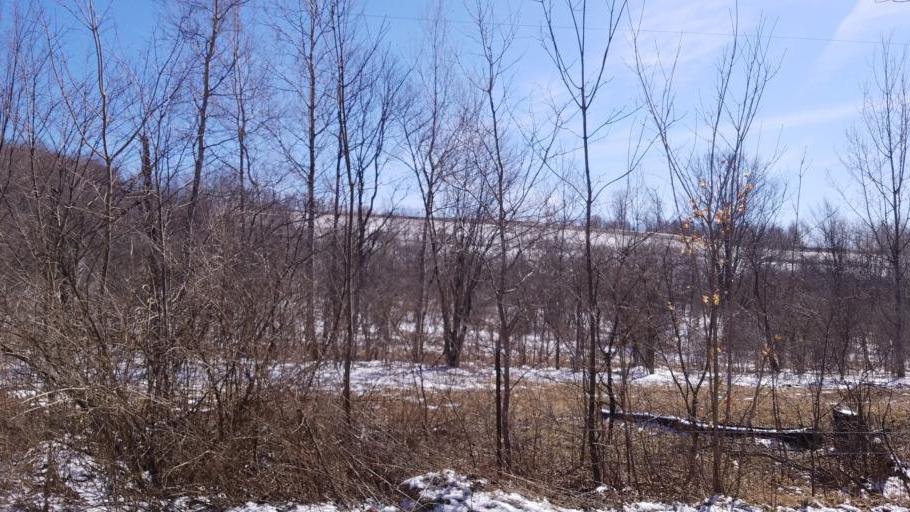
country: US
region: Pennsylvania
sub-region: Tioga County
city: Westfield
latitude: 41.9282
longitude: -77.7542
